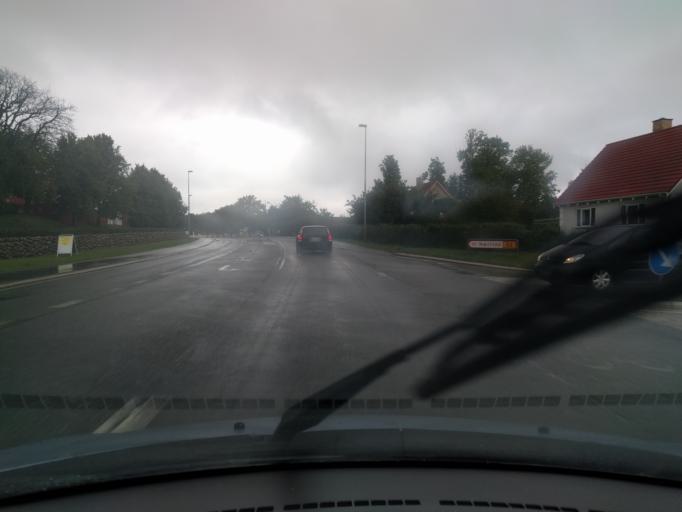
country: DK
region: Zealand
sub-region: Naestved Kommune
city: Naestved
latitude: 55.1571
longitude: 11.8194
